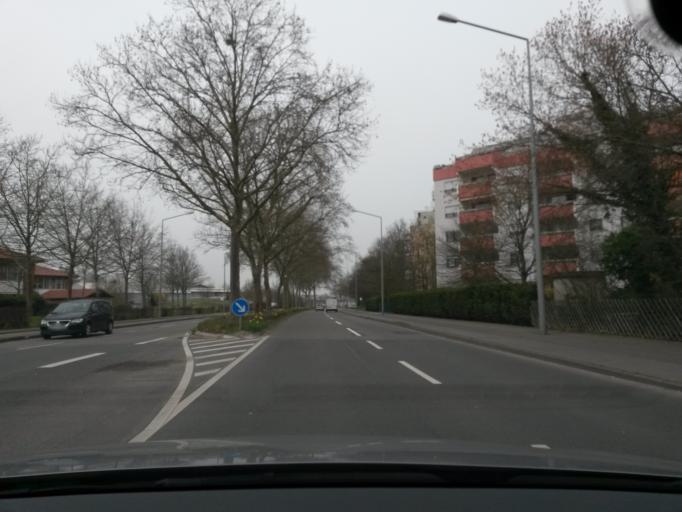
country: DE
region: Rheinland-Pfalz
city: Worms
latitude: 49.6444
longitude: 8.3433
